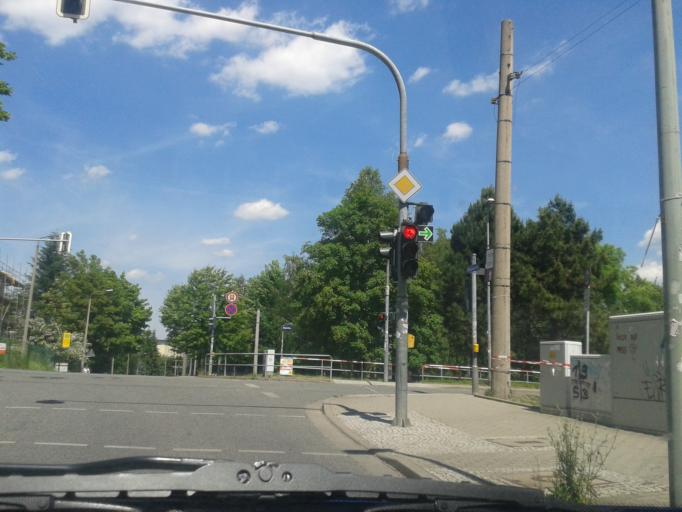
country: DE
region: Saxony
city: Dresden
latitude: 51.0190
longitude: 13.7413
